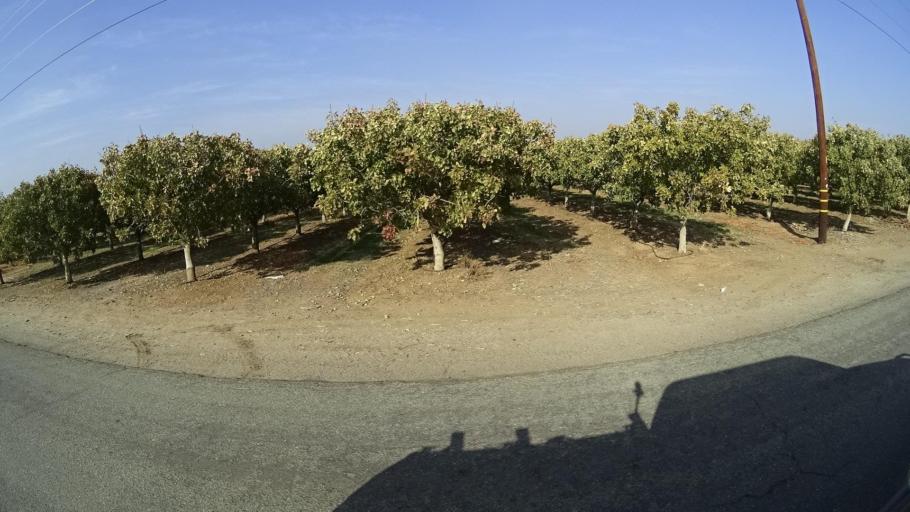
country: US
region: California
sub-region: Tulare County
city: Richgrove
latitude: 35.7907
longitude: -119.0734
